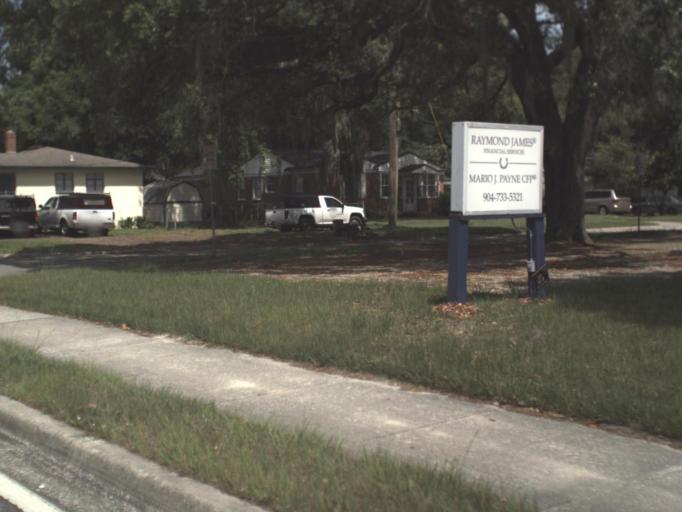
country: US
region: Florida
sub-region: Duval County
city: Jacksonville
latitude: 30.2609
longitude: -81.6392
